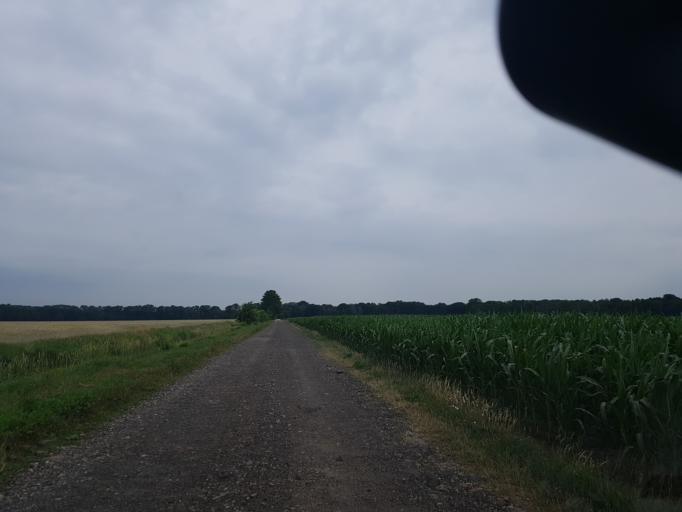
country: DE
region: Brandenburg
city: Schonewalde
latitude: 51.6934
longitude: 13.5428
